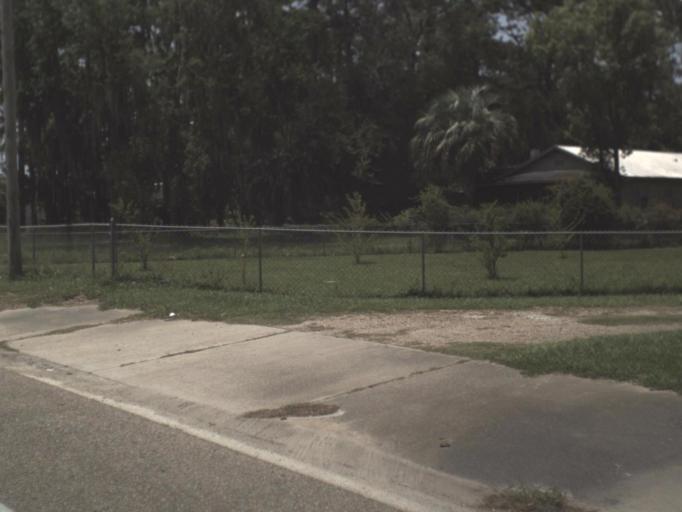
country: US
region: Florida
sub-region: Taylor County
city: Perry
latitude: 30.0704
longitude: -83.5608
